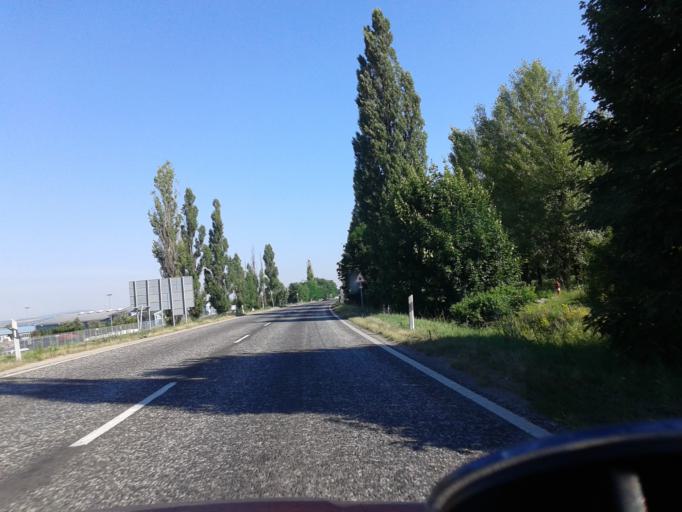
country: HU
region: Pest
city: Biatorbagy
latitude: 47.4773
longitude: 18.8407
